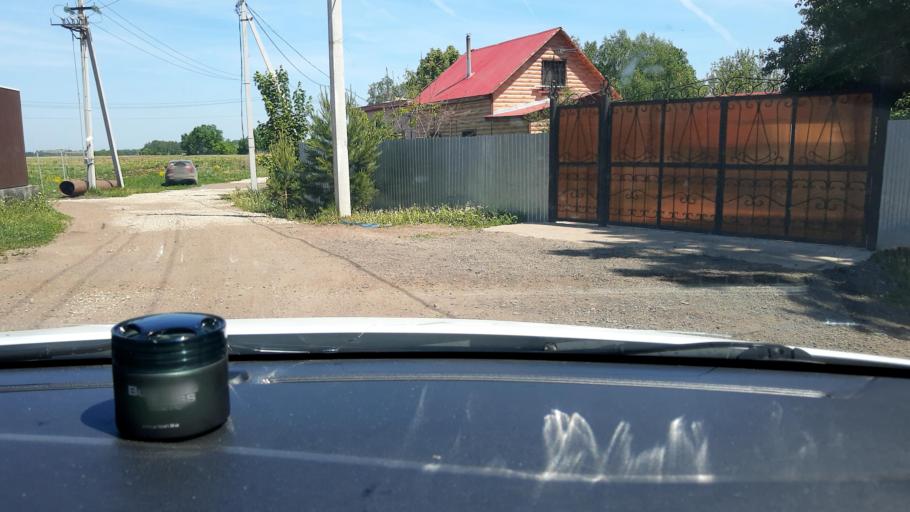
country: RU
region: Bashkortostan
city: Mikhaylovka
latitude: 54.8415
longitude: 55.9492
